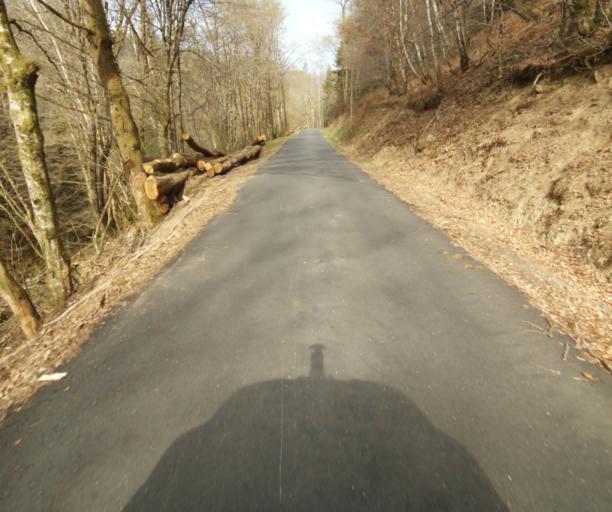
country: FR
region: Limousin
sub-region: Departement de la Correze
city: Chamboulive
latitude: 45.4265
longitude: 1.7932
